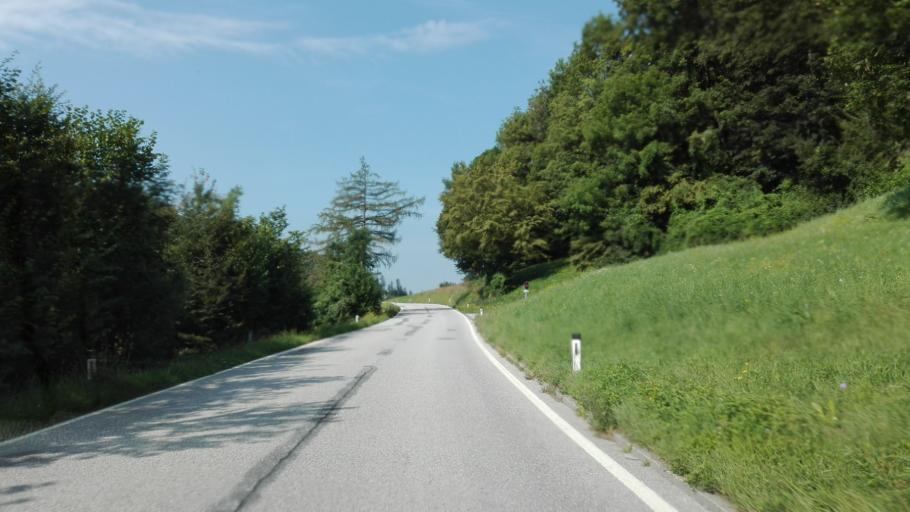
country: AT
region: Lower Austria
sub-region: Politischer Bezirk Lilienfeld
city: Eschenau
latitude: 48.0370
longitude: 15.5228
